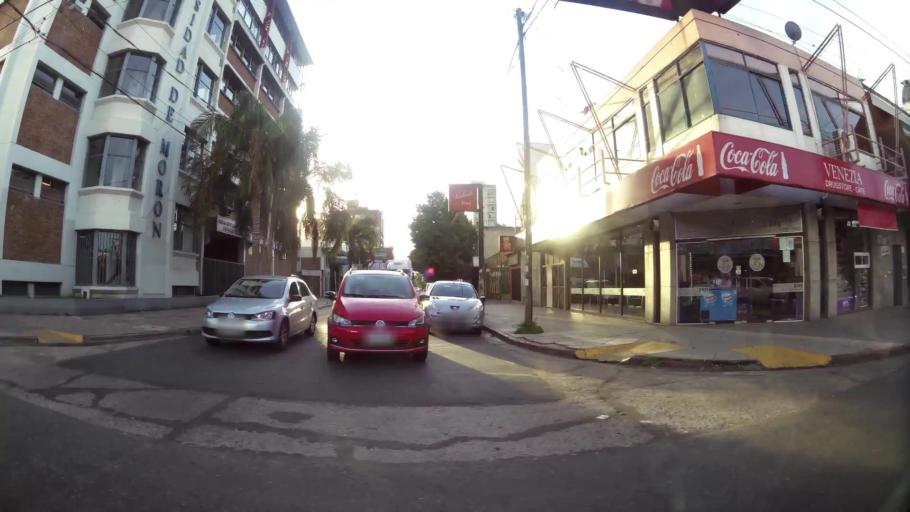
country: AR
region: Buenos Aires
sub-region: Partido de Moron
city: Moron
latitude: -34.6463
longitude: -58.6211
